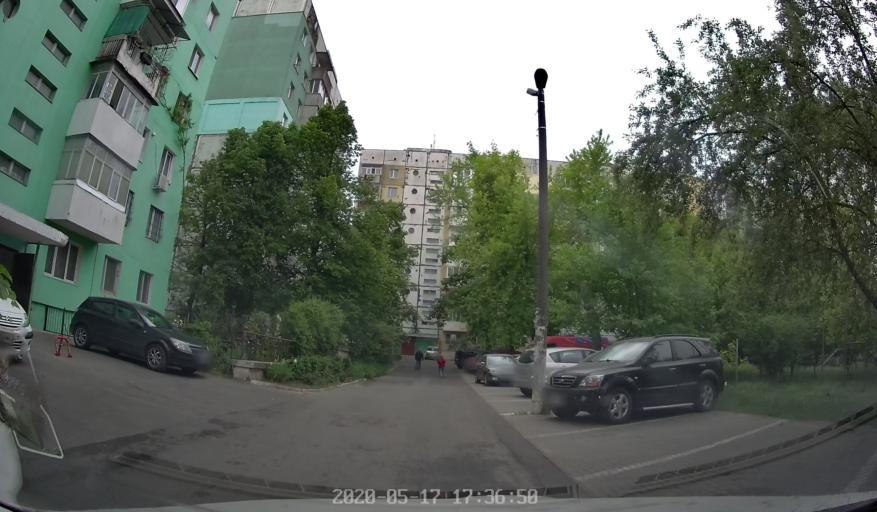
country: MD
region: Chisinau
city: Vatra
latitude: 47.0439
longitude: 28.7887
